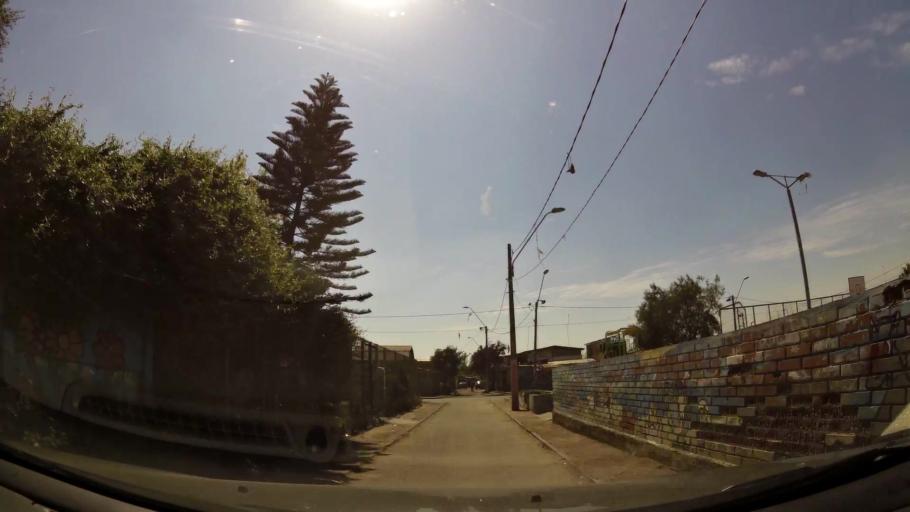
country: CL
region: Santiago Metropolitan
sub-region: Provincia de Santiago
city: La Pintana
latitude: -33.5934
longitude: -70.6092
